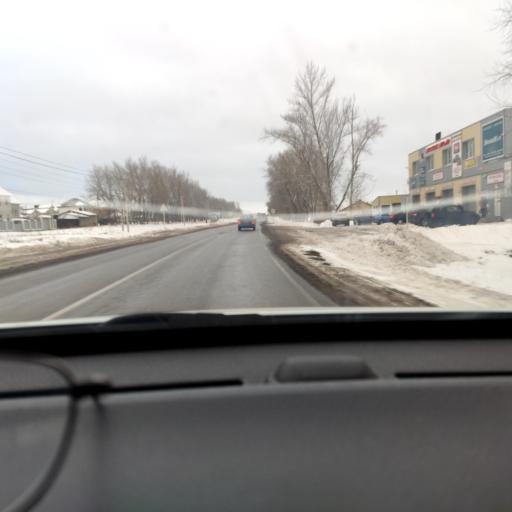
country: RU
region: Voronezj
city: Novaya Usman'
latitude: 51.6673
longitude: 39.4050
